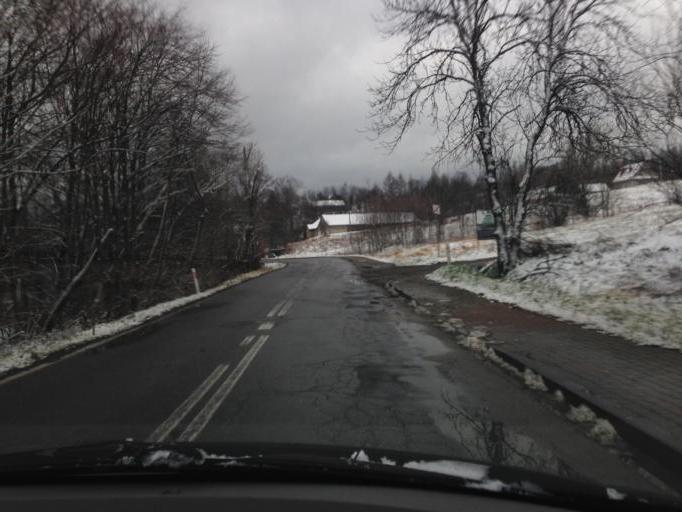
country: PL
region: Lesser Poland Voivodeship
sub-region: Powiat brzeski
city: Iwkowa
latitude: 49.8577
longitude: 20.5508
